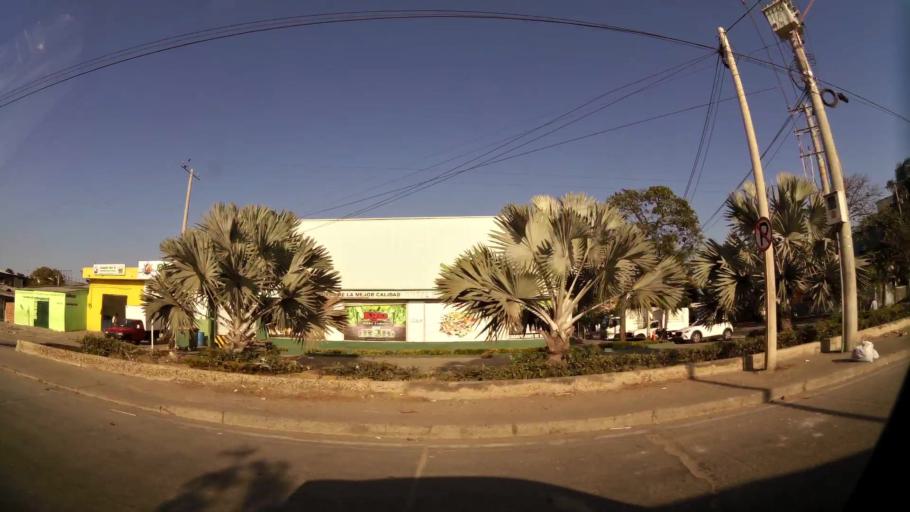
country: CO
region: Bolivar
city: Cartagena
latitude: 10.4100
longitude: -75.5236
